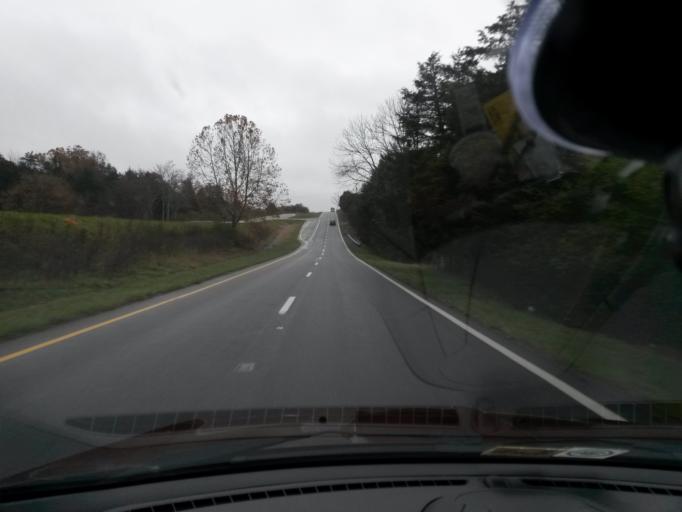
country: US
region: Virginia
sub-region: Botetourt County
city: Fincastle
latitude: 37.5336
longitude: -79.8687
